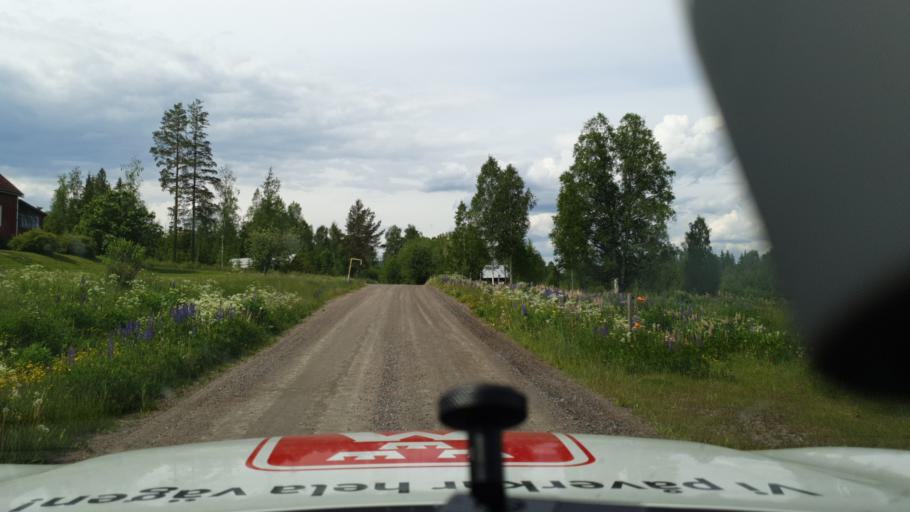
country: SE
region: Vaermland
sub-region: Torsby Kommun
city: Torsby
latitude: 59.9724
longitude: 12.8623
